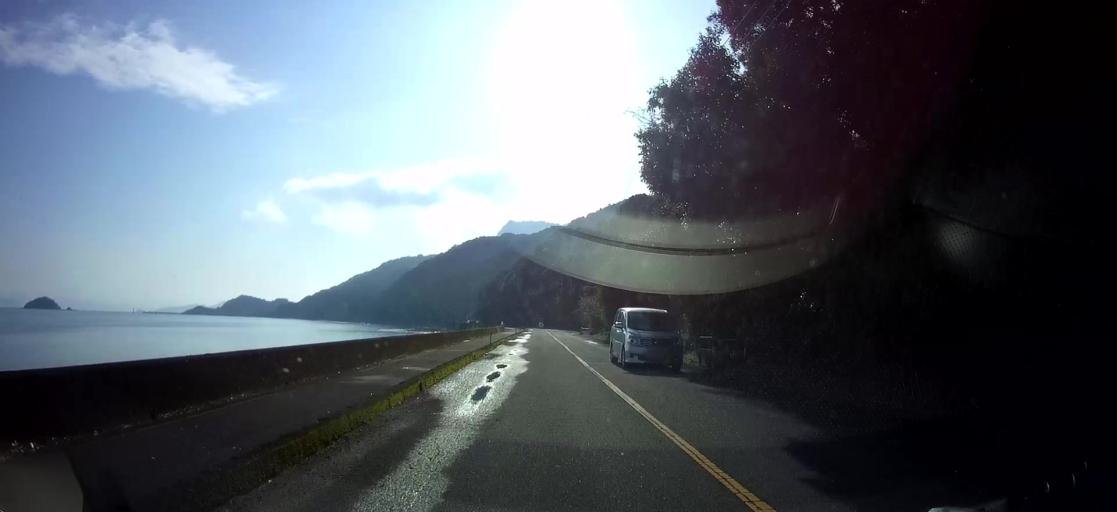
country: JP
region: Kumamoto
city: Yatsushiro
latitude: 32.4894
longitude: 130.4397
